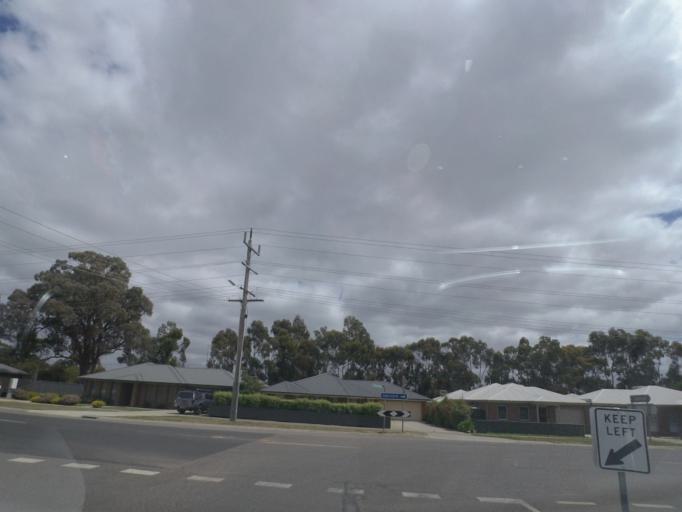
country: AU
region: Victoria
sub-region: Whittlesea
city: Whittlesea
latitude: -37.2078
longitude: 145.0443
